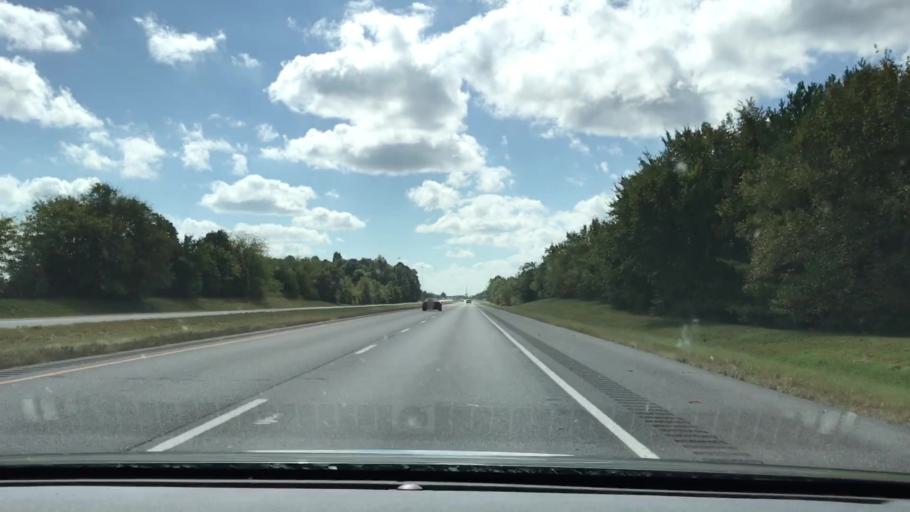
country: US
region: Kentucky
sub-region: McCracken County
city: Reidland
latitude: 37.0019
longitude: -88.5069
